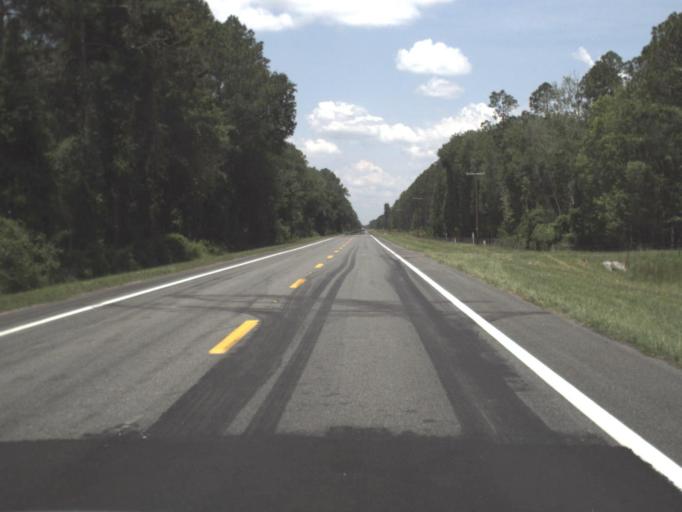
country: US
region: Florida
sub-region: Union County
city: Lake Butler
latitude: 30.0408
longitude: -82.3845
